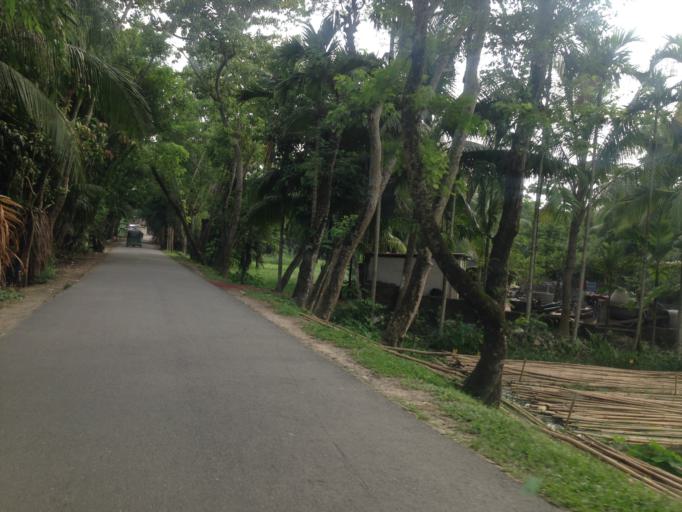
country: BD
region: Chittagong
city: Raipur
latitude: 23.0314
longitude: 90.7095
